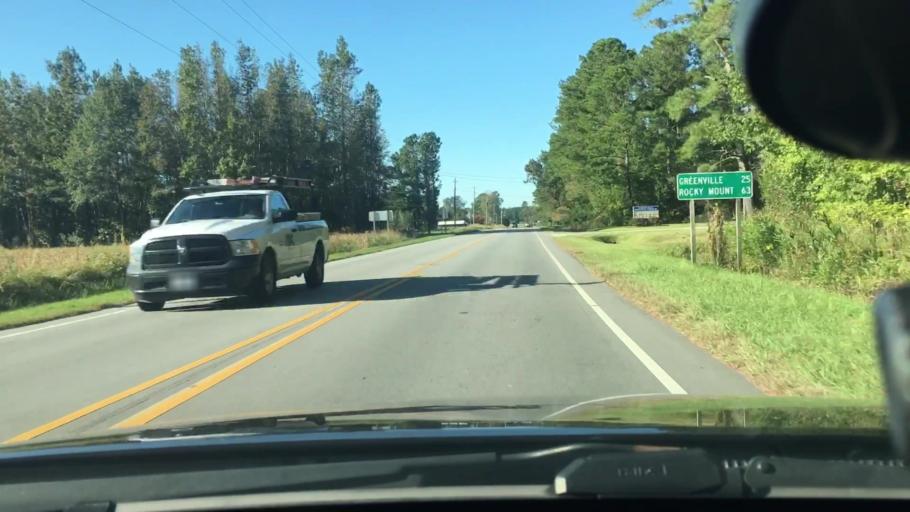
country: US
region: North Carolina
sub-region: Craven County
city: Vanceboro
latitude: 35.3133
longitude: -77.1616
